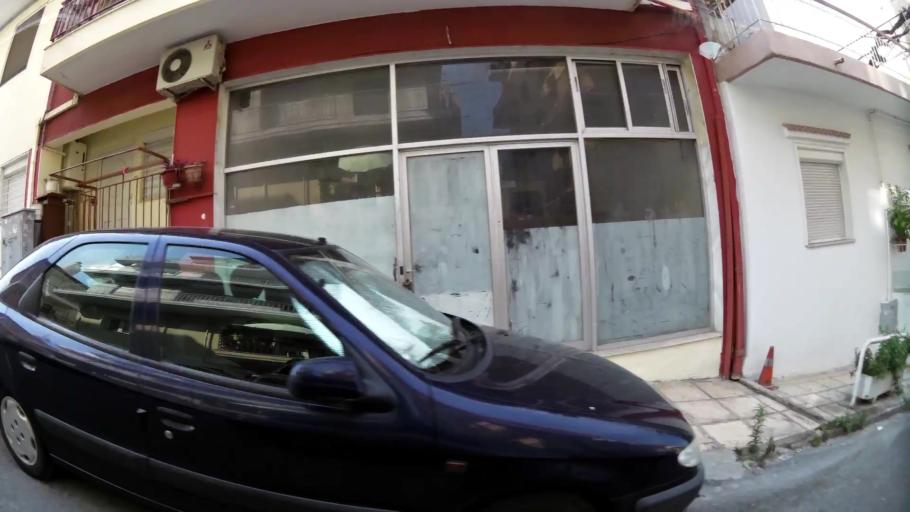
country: GR
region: Central Macedonia
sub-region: Nomos Thessalonikis
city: Sykies
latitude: 40.6548
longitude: 22.9406
